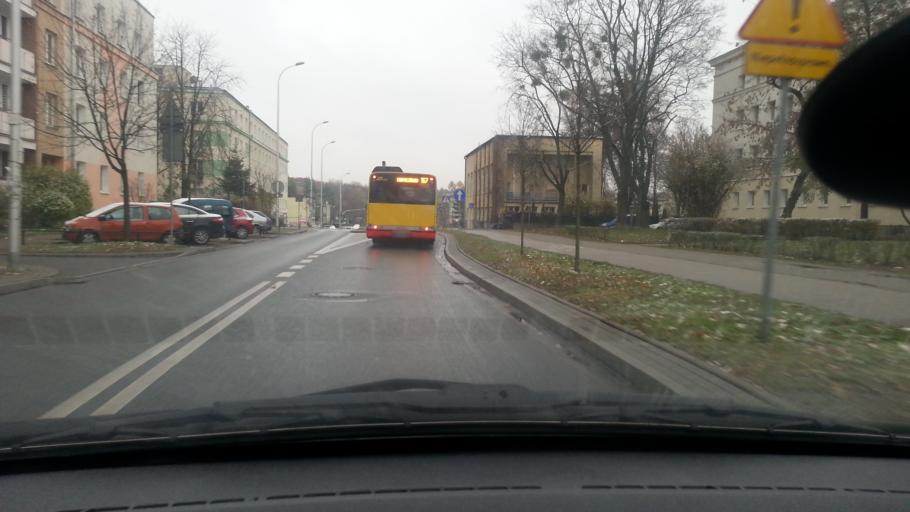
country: PL
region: Masovian Voivodeship
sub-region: Warszawa
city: Bemowo
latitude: 52.2456
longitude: 20.9478
